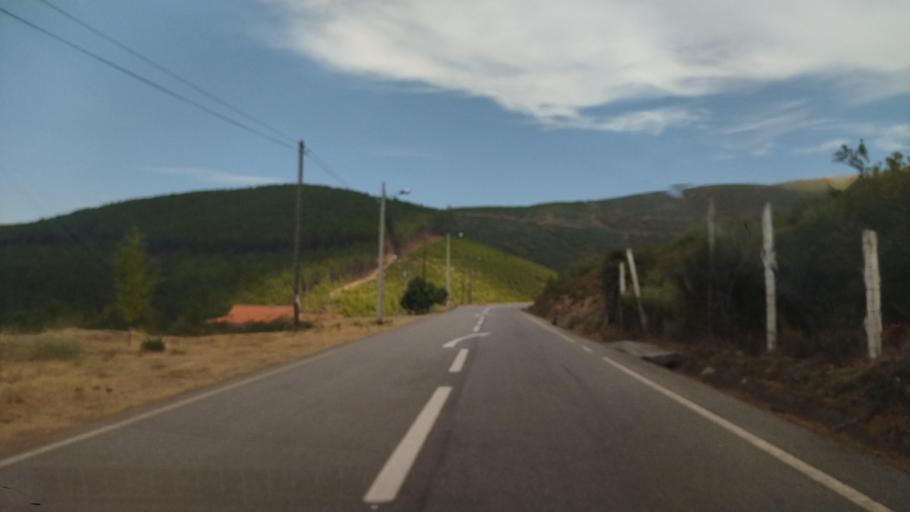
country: PT
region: Castelo Branco
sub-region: Covilha
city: Teixoso
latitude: 40.3757
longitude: -7.4576
